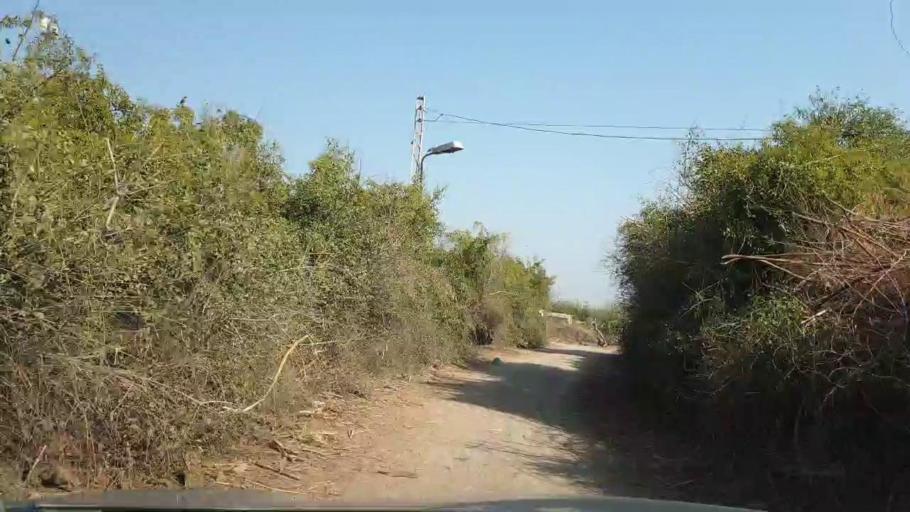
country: PK
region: Sindh
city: Mirpur Khas
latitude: 25.6469
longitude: 68.9100
